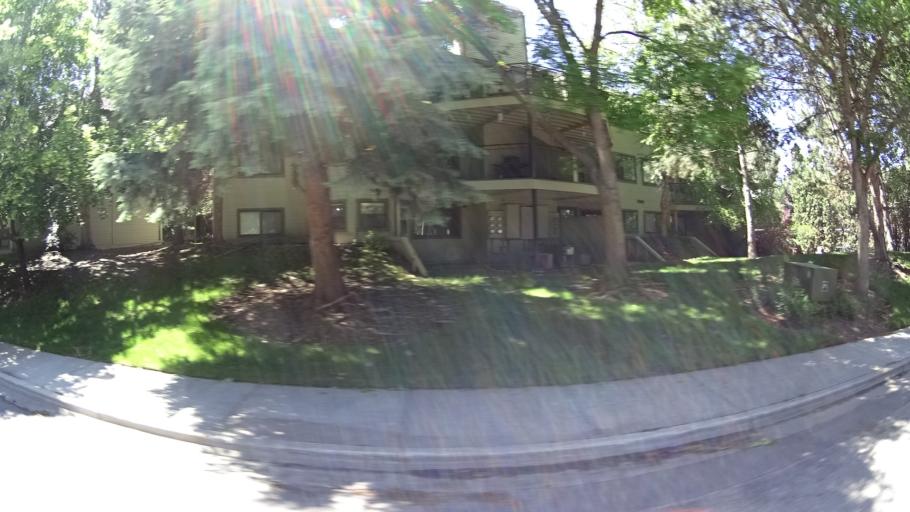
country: US
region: Idaho
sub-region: Ada County
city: Boise
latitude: 43.5695
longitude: -116.1819
